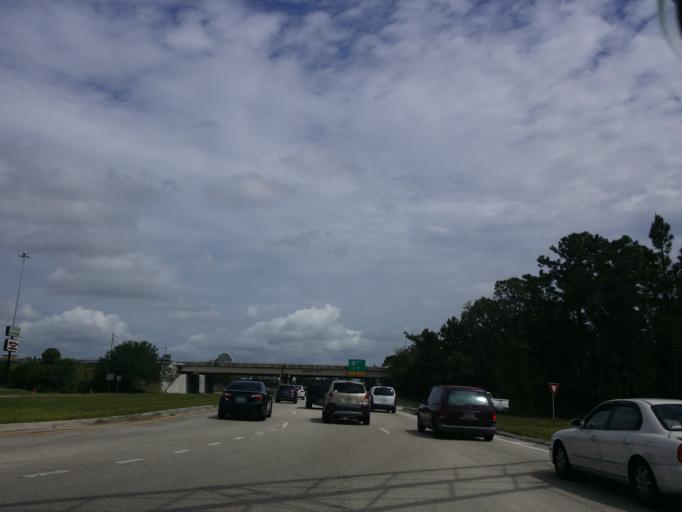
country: US
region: Florida
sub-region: Orange County
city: Williamsburg
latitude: 28.4194
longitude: -81.4598
